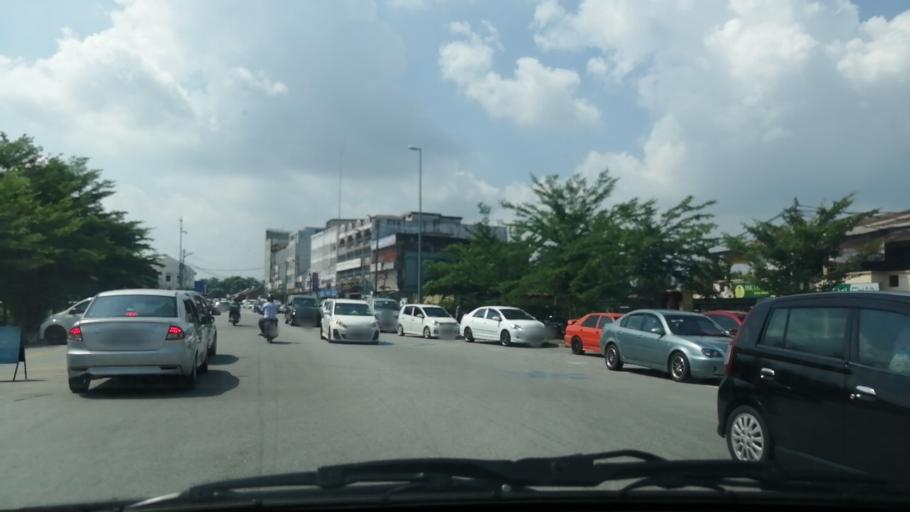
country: MY
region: Kedah
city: Sungai Petani
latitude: 5.6404
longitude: 100.4906
